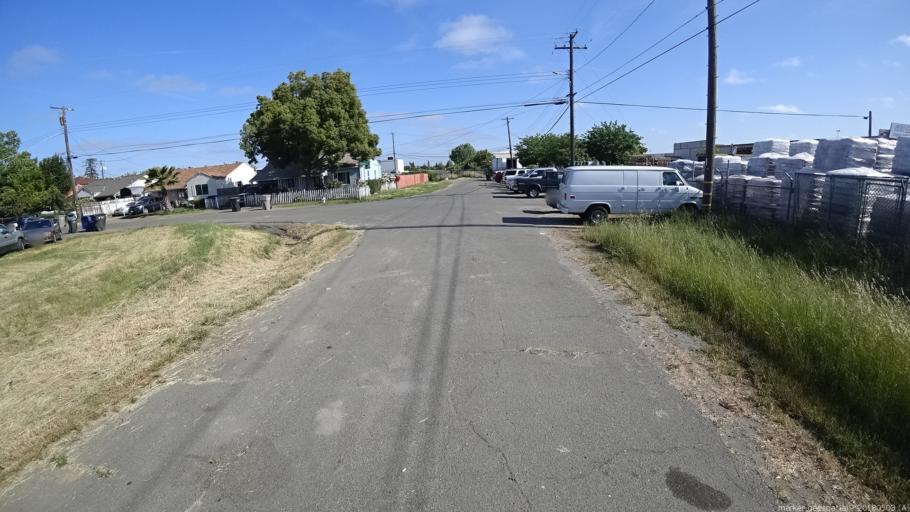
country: US
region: California
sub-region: Sacramento County
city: Arden-Arcade
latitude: 38.6118
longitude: -121.4359
